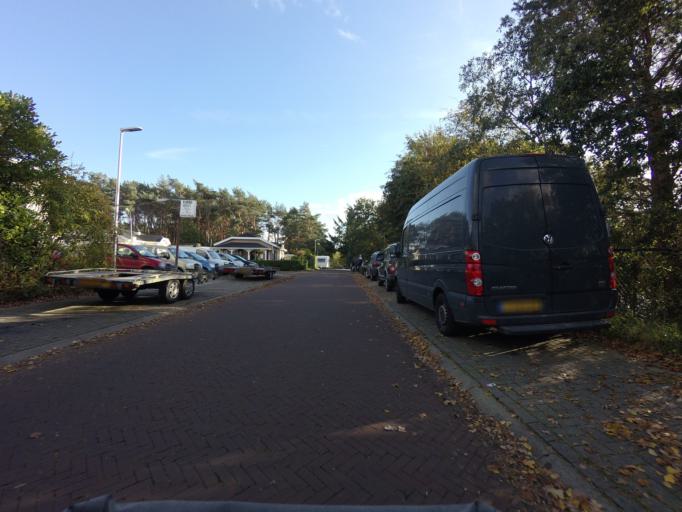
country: NL
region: North Holland
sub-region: Gemeente Bussum
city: Bussum
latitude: 52.2604
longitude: 5.1697
